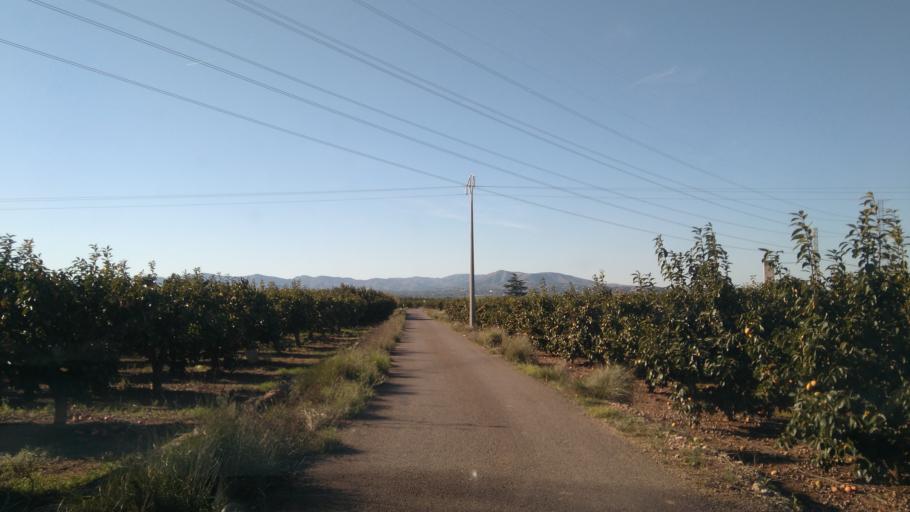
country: ES
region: Valencia
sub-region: Provincia de Valencia
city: L'Alcudia
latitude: 39.1852
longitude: -0.5215
